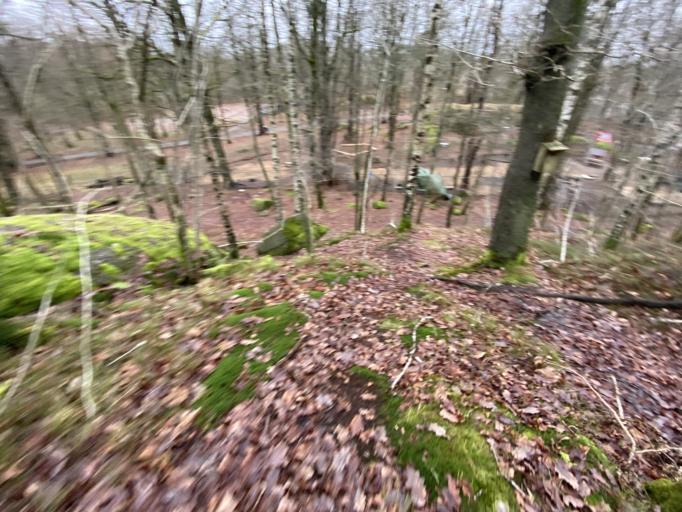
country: SE
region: Vaestra Goetaland
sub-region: Goteborg
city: Eriksbo
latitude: 57.7175
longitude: 12.0452
